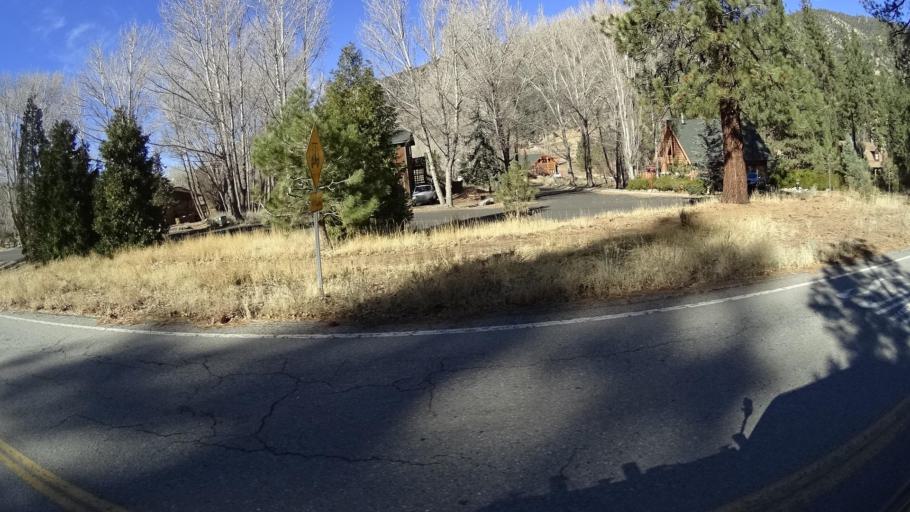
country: US
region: California
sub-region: Kern County
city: Pine Mountain Club
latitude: 34.8522
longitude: -119.1645
